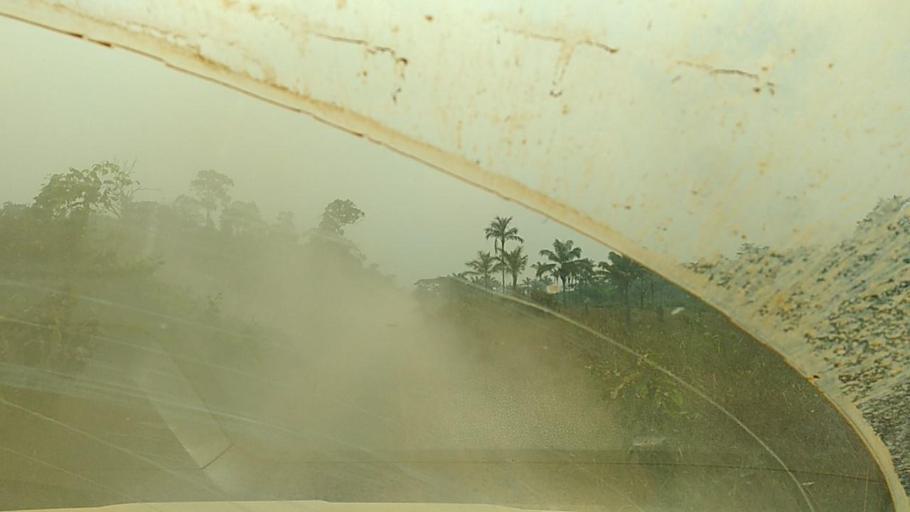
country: BR
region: Rondonia
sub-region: Porto Velho
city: Porto Velho
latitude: -8.7721
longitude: -63.1810
